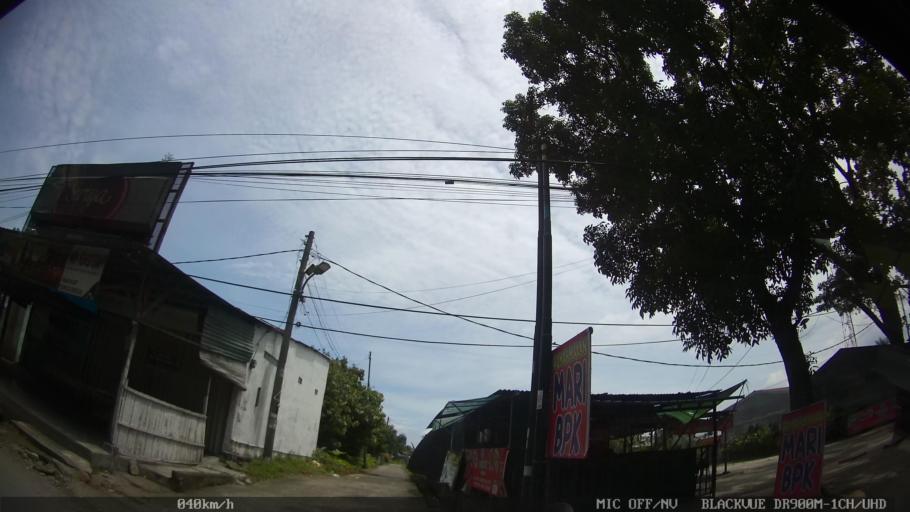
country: ID
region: North Sumatra
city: Sunggal
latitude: 3.5408
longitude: 98.6387
